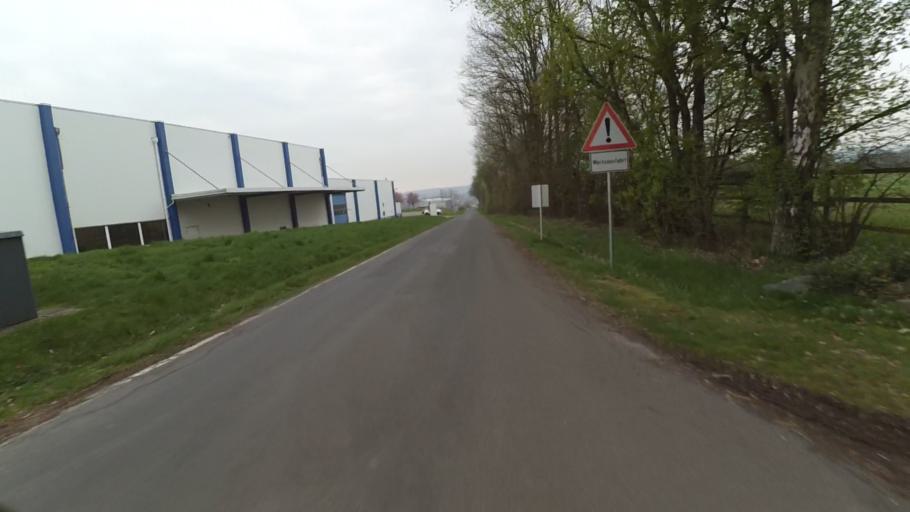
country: DE
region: Rheinland-Pfalz
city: Bannberscheid
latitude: 50.4541
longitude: 7.8297
